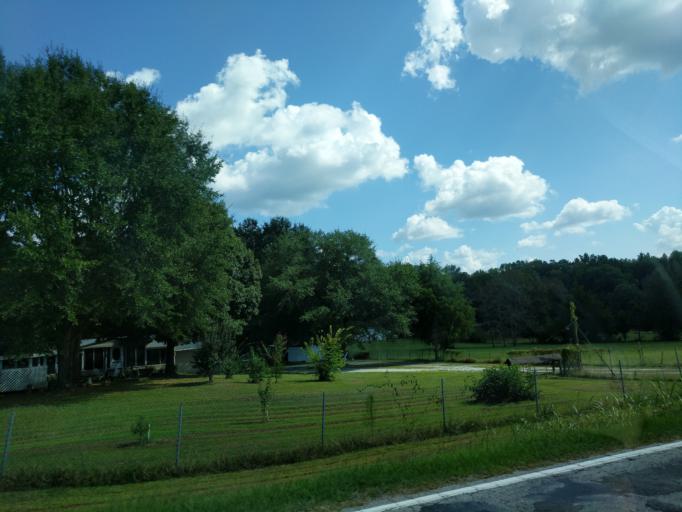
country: US
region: South Carolina
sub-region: Spartanburg County
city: Woodruff
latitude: 34.7047
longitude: -82.0490
